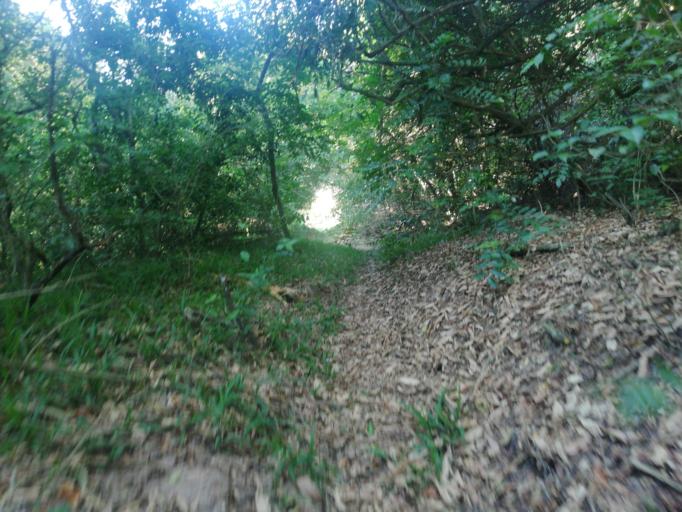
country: AR
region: Corrientes
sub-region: Departamento de San Miguel
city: San Miguel
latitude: -27.9890
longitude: -57.5404
